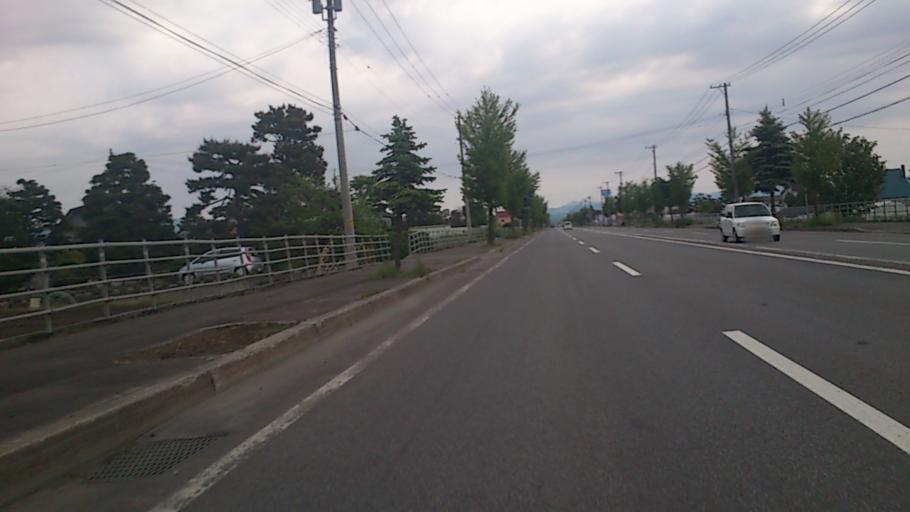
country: JP
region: Hokkaido
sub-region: Asahikawa-shi
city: Asahikawa
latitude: 43.8288
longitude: 142.4633
